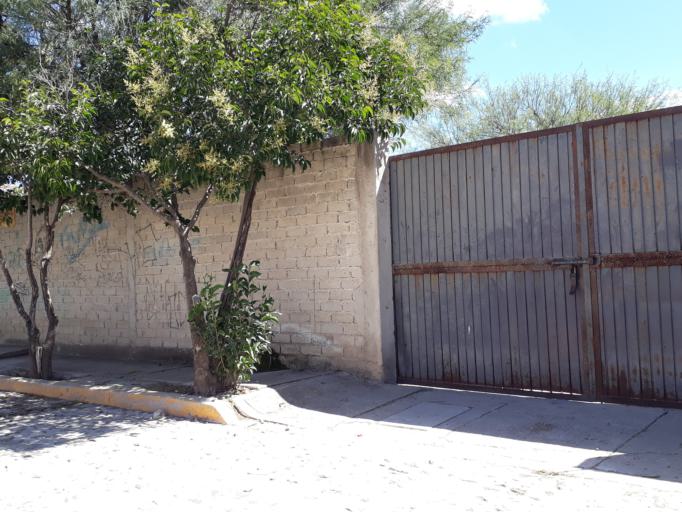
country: MX
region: Aguascalientes
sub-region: Aguascalientes
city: San Sebastian [Fraccionamiento]
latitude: 21.8026
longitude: -102.2748
